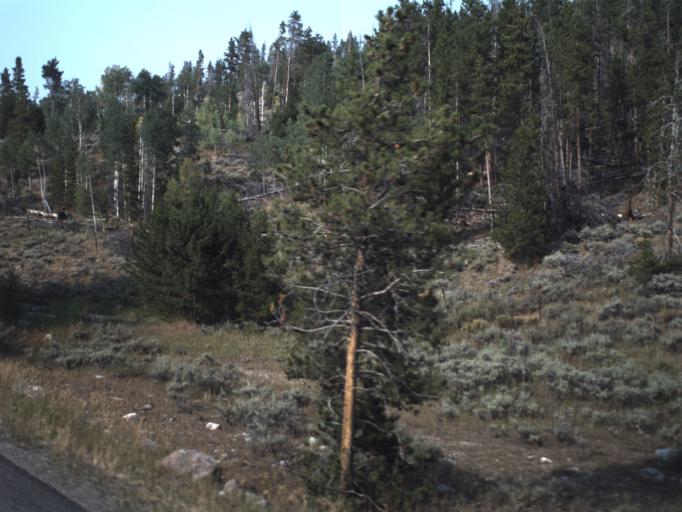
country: US
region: Wyoming
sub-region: Uinta County
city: Evanston
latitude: 40.9288
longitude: -110.8292
